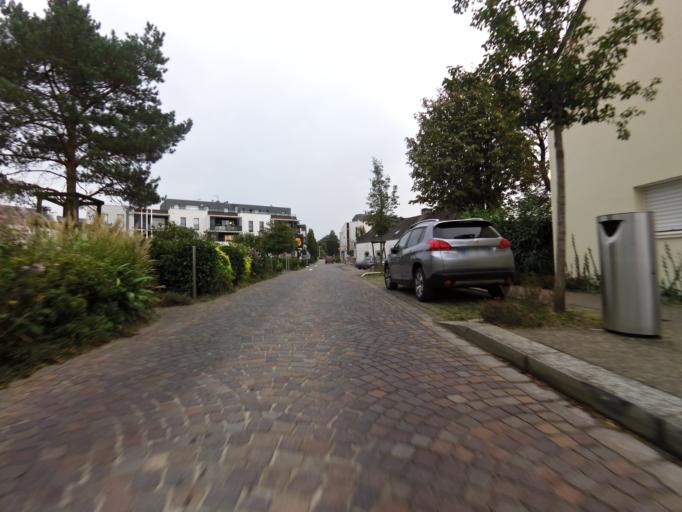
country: FR
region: Brittany
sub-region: Departement du Morbihan
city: Plescop
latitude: 47.6979
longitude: -2.8050
